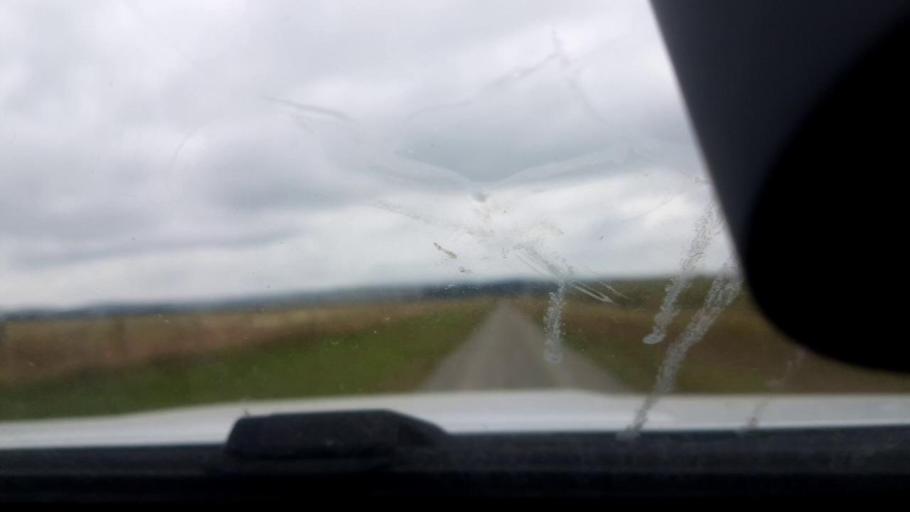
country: NZ
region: Canterbury
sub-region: Timaru District
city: Pleasant Point
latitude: -44.2335
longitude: 171.1675
